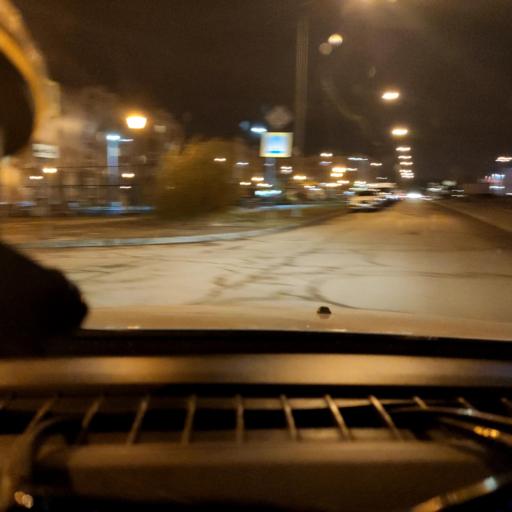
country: RU
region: Samara
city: Samara
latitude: 53.1158
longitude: 50.1628
